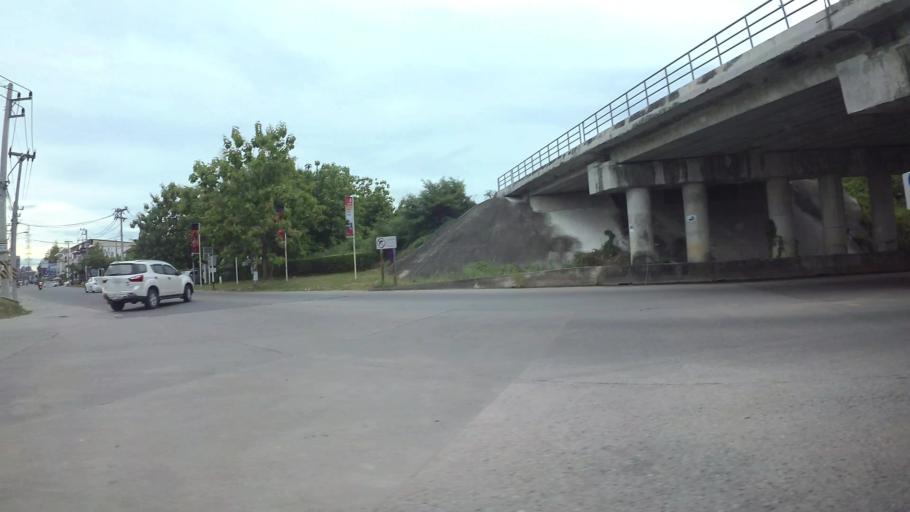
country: TH
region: Chon Buri
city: Si Racha
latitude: 13.1502
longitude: 100.9455
